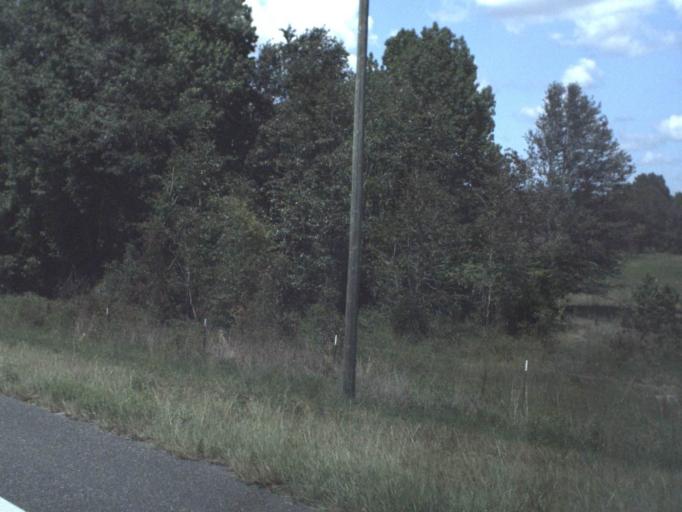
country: US
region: Florida
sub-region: Alachua County
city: High Springs
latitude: 29.7692
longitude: -82.7407
